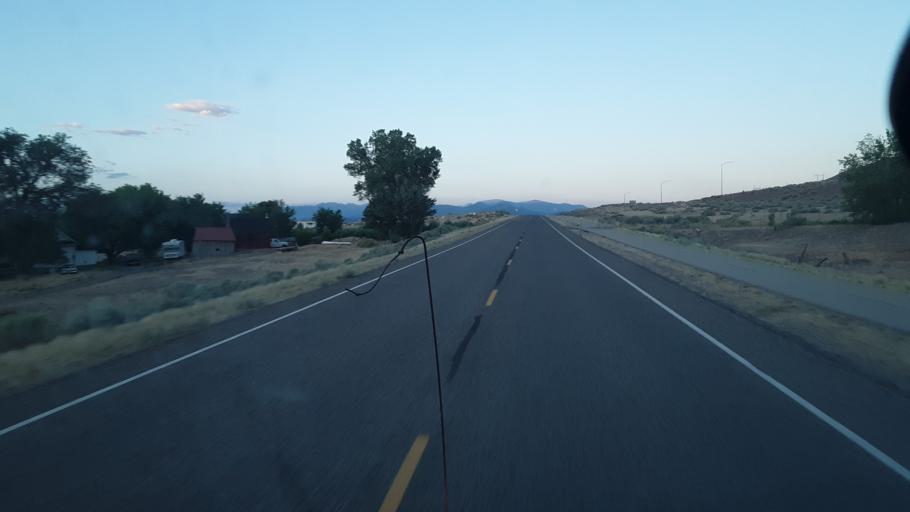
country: US
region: Utah
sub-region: Sevier County
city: Monroe
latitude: 38.6787
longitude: -112.1574
